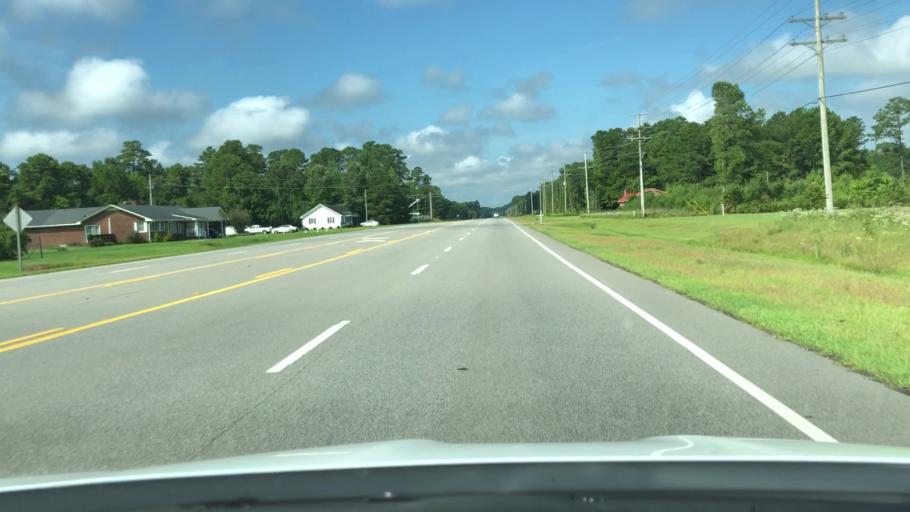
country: US
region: North Carolina
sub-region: Bertie County
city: Windsor
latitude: 36.0243
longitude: -76.8145
